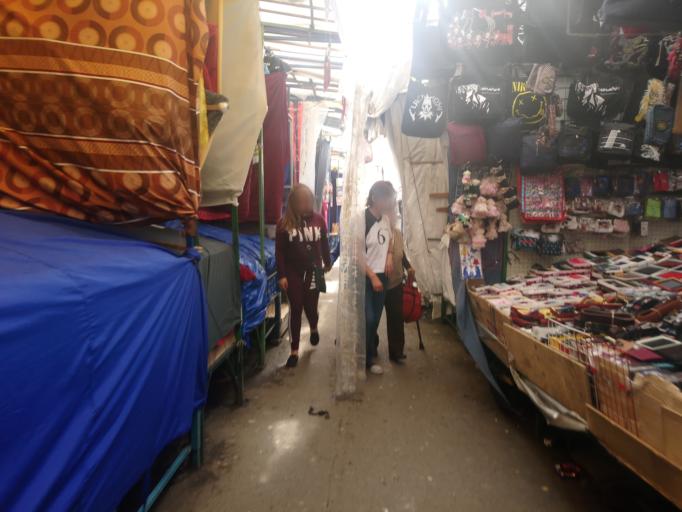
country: BO
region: La Paz
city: La Paz
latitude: -16.4939
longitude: -68.1457
